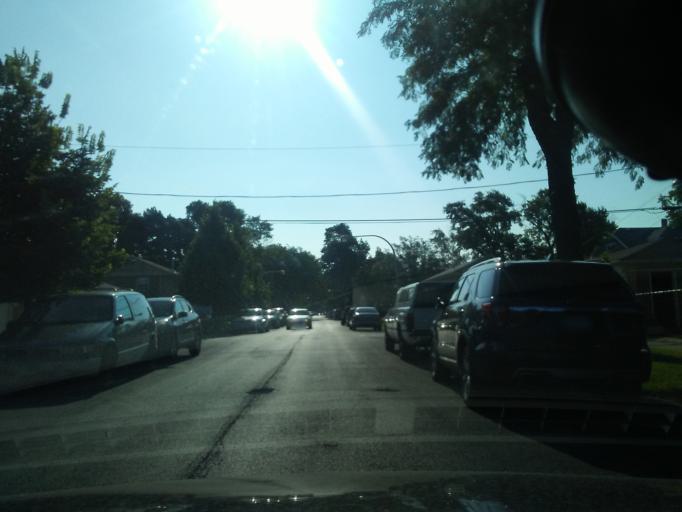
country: US
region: Illinois
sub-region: Cook County
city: Elmwood Park
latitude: 41.9257
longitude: -87.7694
